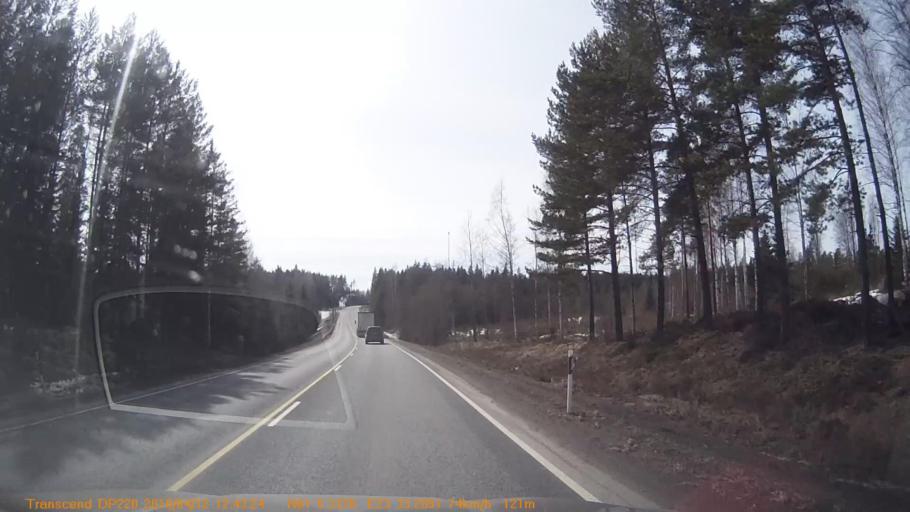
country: FI
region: Pirkanmaa
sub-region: Etelae-Pirkanmaa
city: Urjala
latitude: 61.0889
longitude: 23.5533
